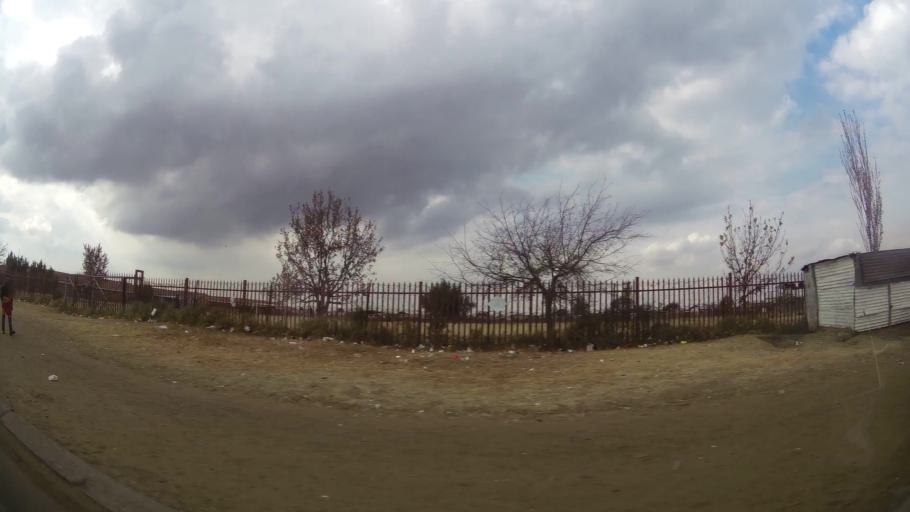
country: ZA
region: Orange Free State
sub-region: Fezile Dabi District Municipality
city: Sasolburg
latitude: -26.8543
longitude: 27.8551
